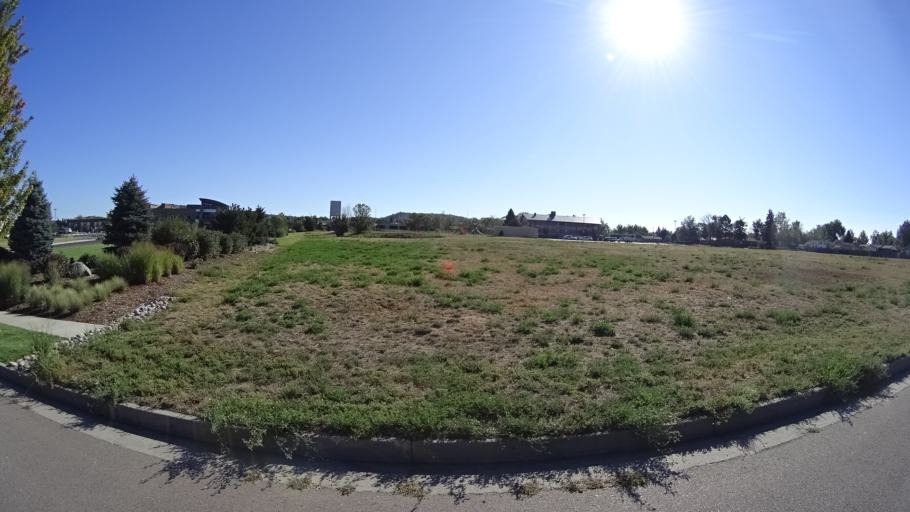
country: US
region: Colorado
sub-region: El Paso County
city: Colorado Springs
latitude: 38.8705
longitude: -104.7968
